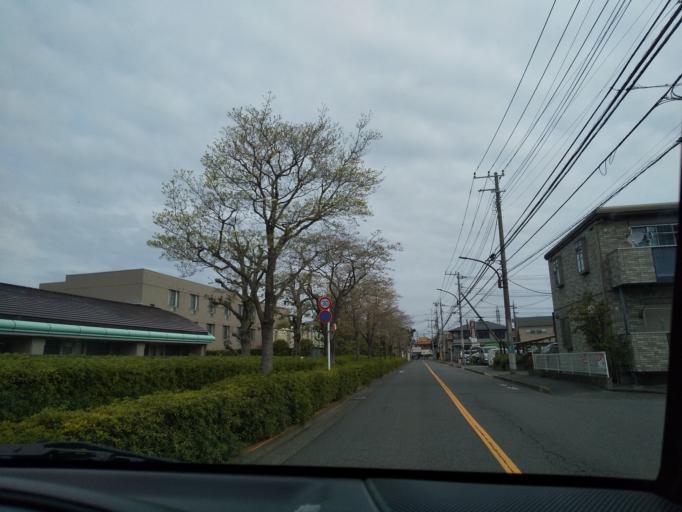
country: JP
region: Tokyo
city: Kokubunji
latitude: 35.6822
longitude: 139.4570
